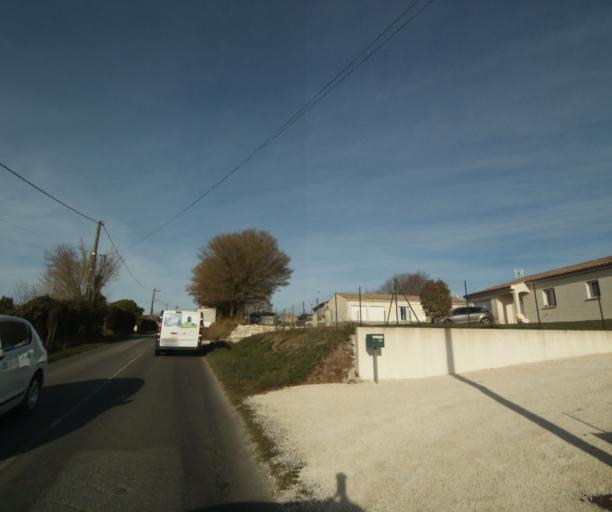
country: FR
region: Poitou-Charentes
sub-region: Departement de la Charente-Maritime
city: Chaniers
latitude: 45.7299
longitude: -0.5580
